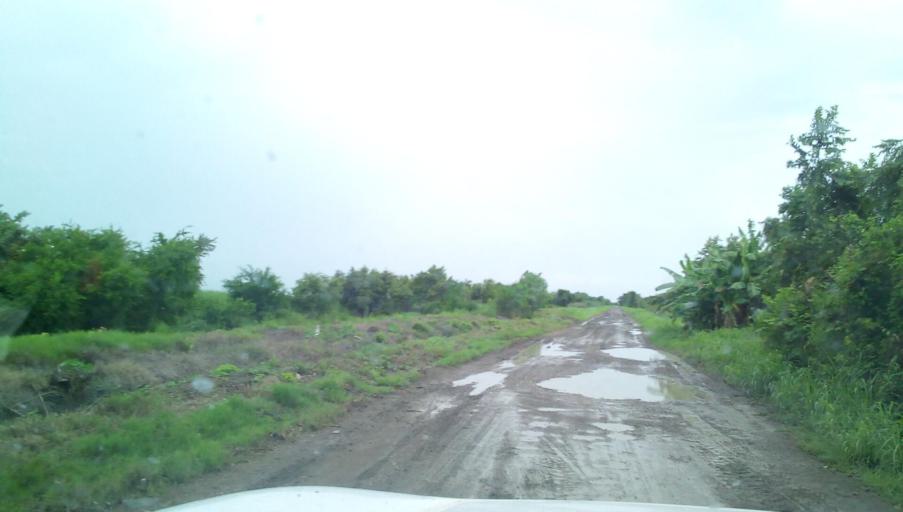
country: MX
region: Veracruz
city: Panuco
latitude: 21.8293
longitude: -98.1106
